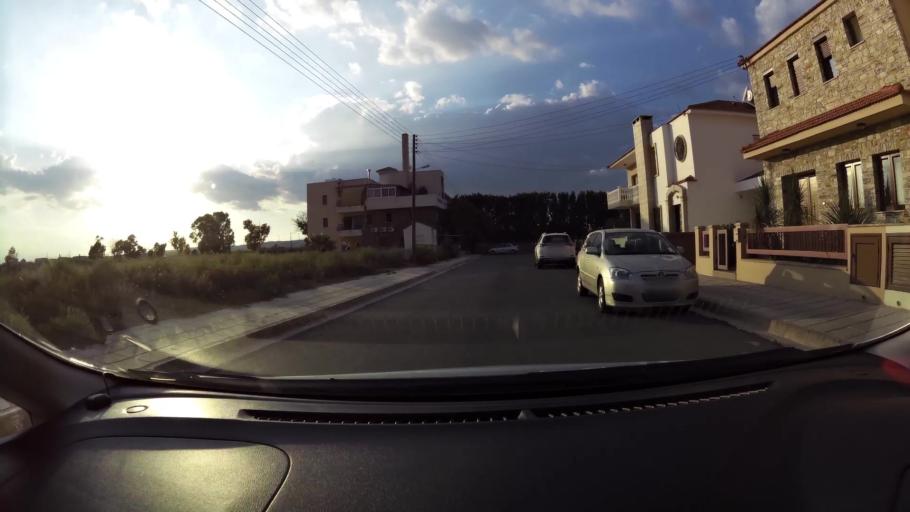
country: CY
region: Larnaka
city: Meneou
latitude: 34.8626
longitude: 33.5830
